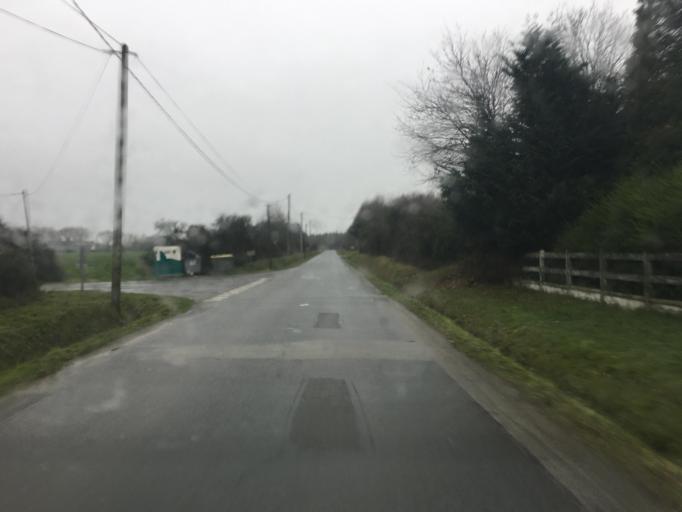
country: FR
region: Brittany
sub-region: Departement du Morbihan
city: Sarzeau
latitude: 47.5300
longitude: -2.6968
